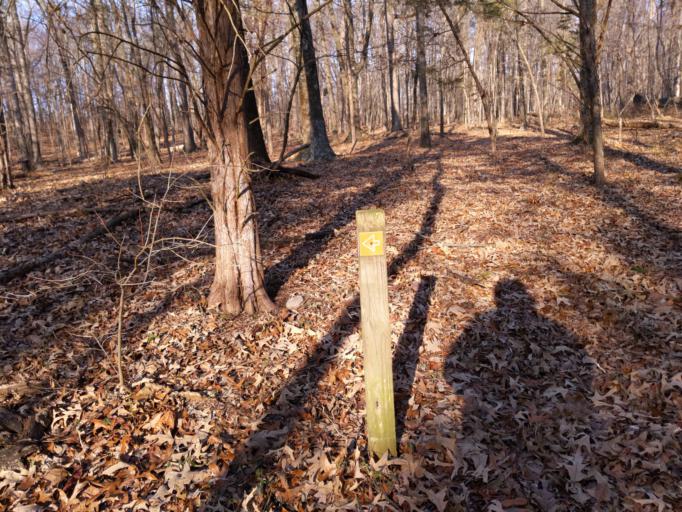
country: US
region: Virginia
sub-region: Loudoun County
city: Dulles Town Center
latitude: 39.0197
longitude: -77.4008
